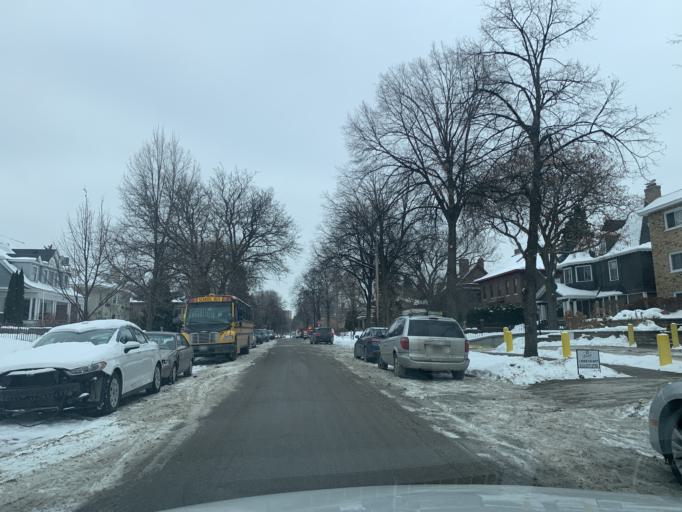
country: US
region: Minnesota
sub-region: Hennepin County
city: Minneapolis
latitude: 44.9581
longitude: -93.2813
